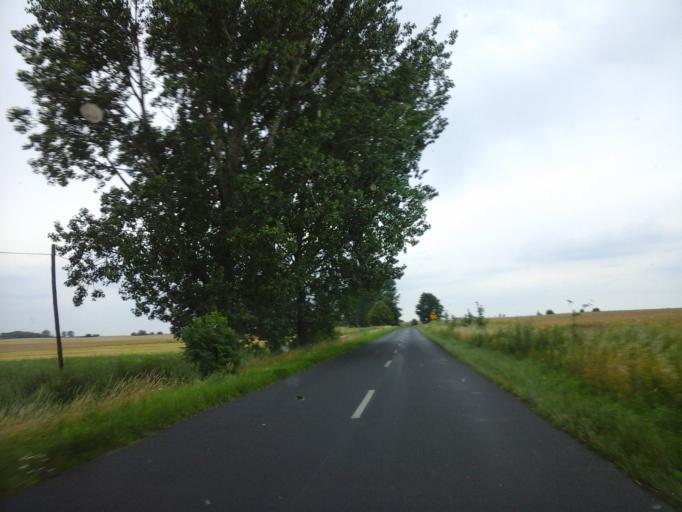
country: PL
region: West Pomeranian Voivodeship
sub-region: Powiat choszczenski
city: Krzecin
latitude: 53.0937
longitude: 15.4715
